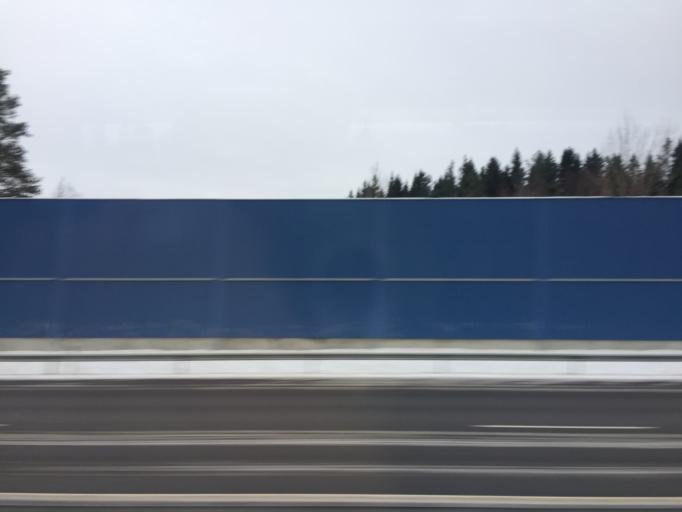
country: FI
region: Kymenlaakso
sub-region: Kotka-Hamina
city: Pyhtaeae
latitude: 60.4863
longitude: 26.5387
